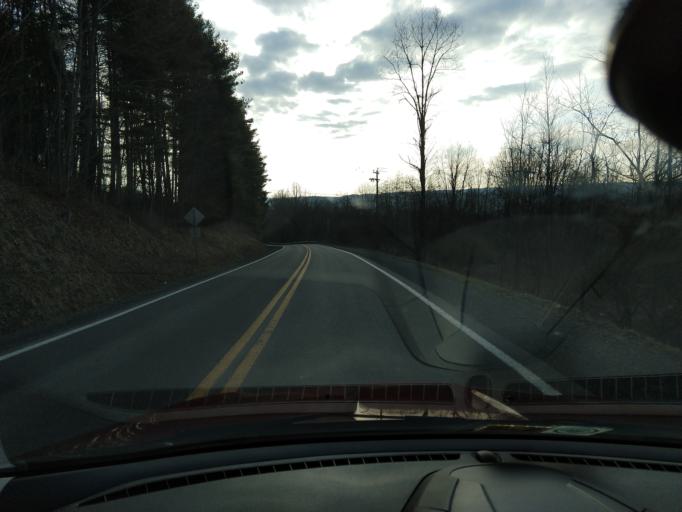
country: US
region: West Virginia
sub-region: Pocahontas County
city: Marlinton
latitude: 38.1172
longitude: -80.2563
